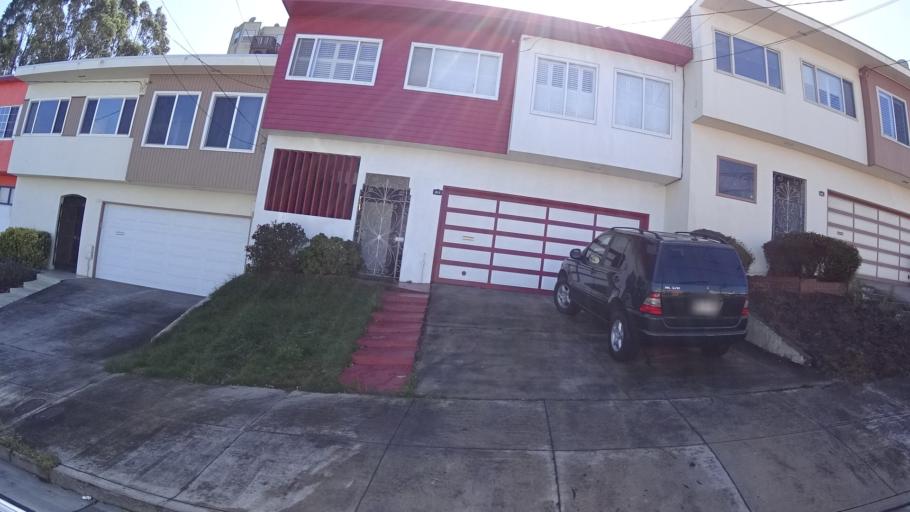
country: US
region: California
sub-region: San Mateo County
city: Daly City
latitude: 37.7028
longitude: -122.4522
